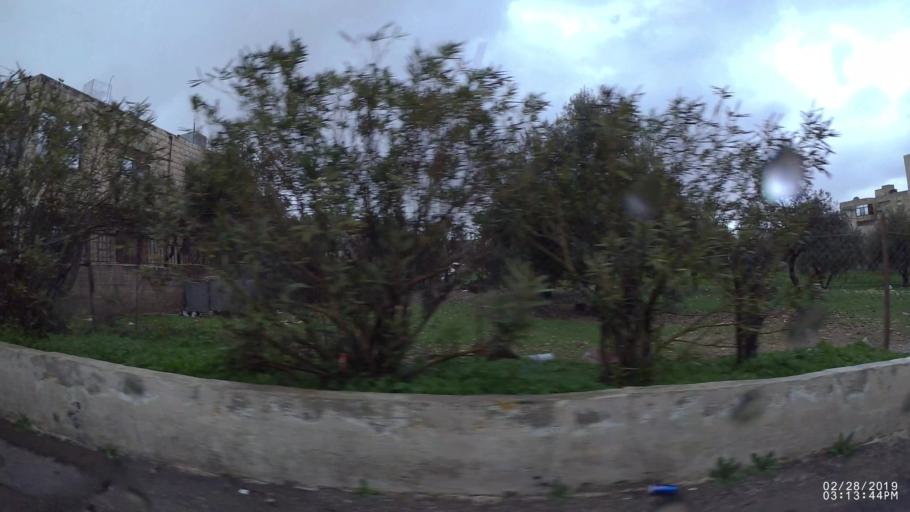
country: JO
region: Amman
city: Al Jubayhah
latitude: 32.0271
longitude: 35.8644
